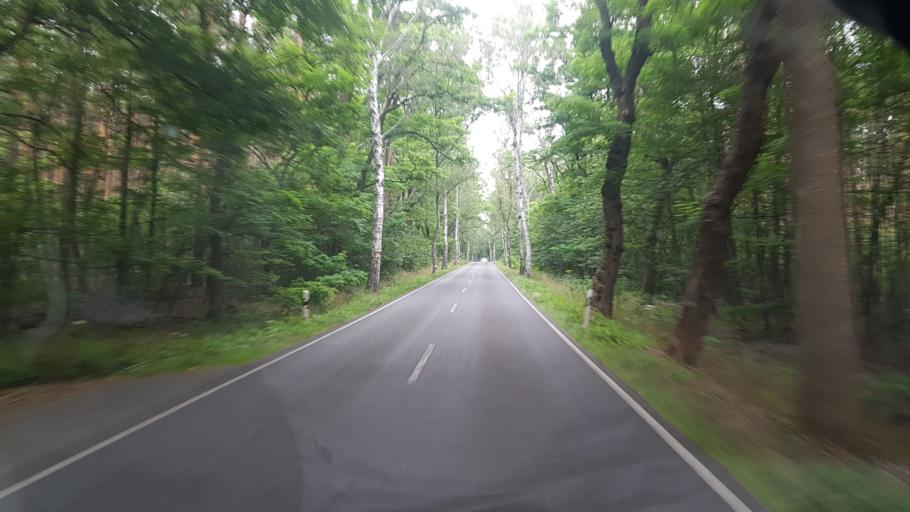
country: DE
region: Brandenburg
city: Schlieben
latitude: 51.7690
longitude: 13.3669
